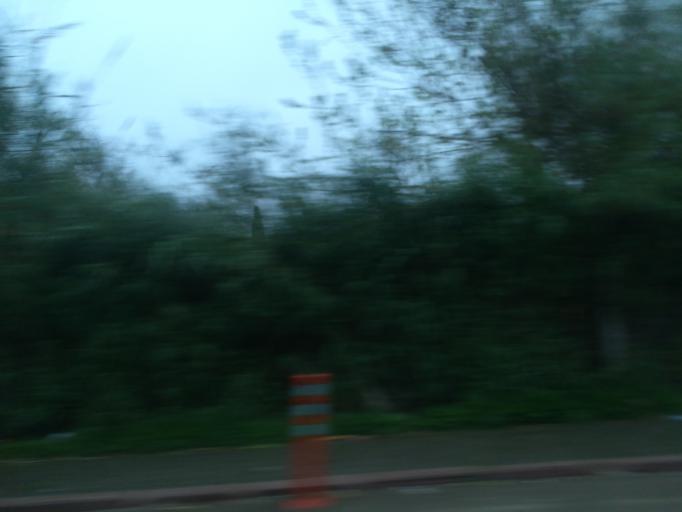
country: TR
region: Adana
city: Seyhan
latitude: 37.0068
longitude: 35.2804
